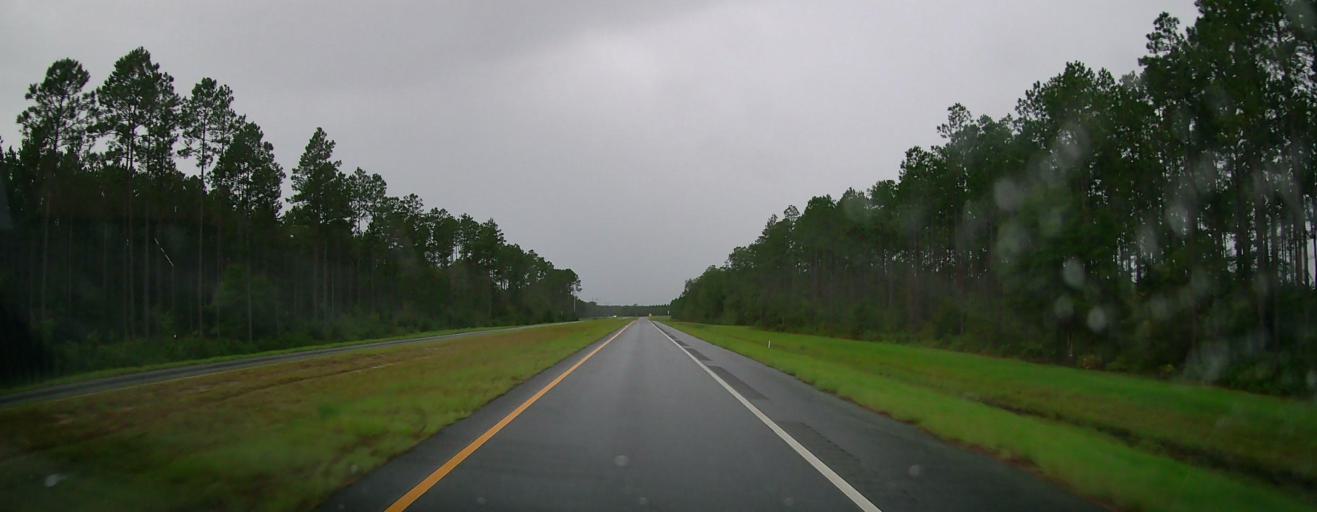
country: US
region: Georgia
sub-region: Clinch County
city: Homerville
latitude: 31.0746
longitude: -82.6558
